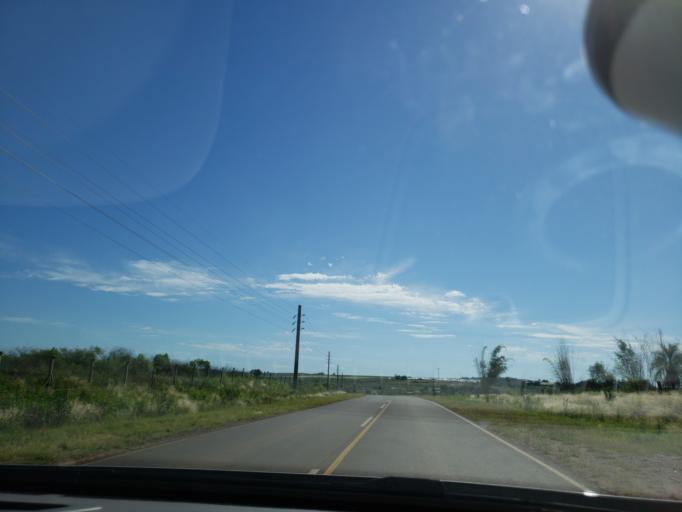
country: AR
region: Misiones
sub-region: Departamento de Capital
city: Posadas
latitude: -27.3878
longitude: -55.9781
